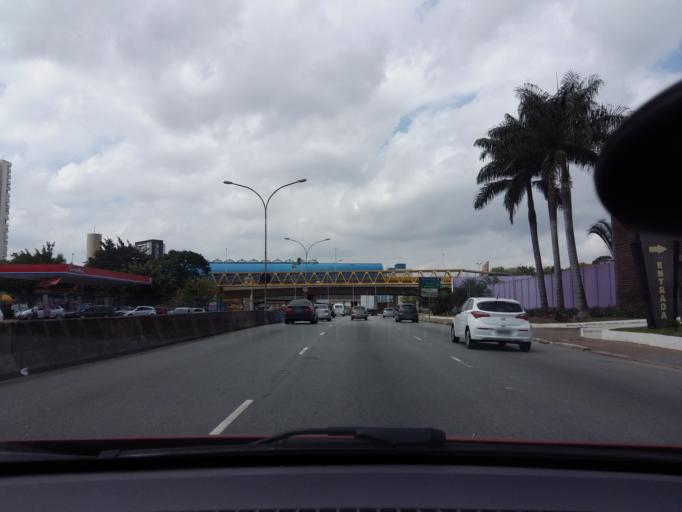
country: BR
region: Sao Paulo
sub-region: Sao Caetano Do Sul
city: Sao Caetano do Sul
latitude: -23.6049
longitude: -46.6040
